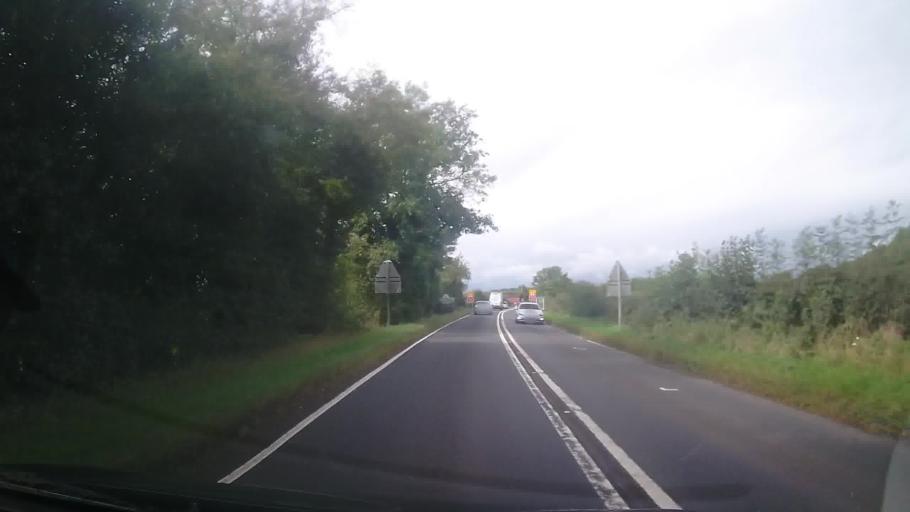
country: GB
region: England
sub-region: Shropshire
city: Romsley
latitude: 52.4365
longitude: -2.3218
